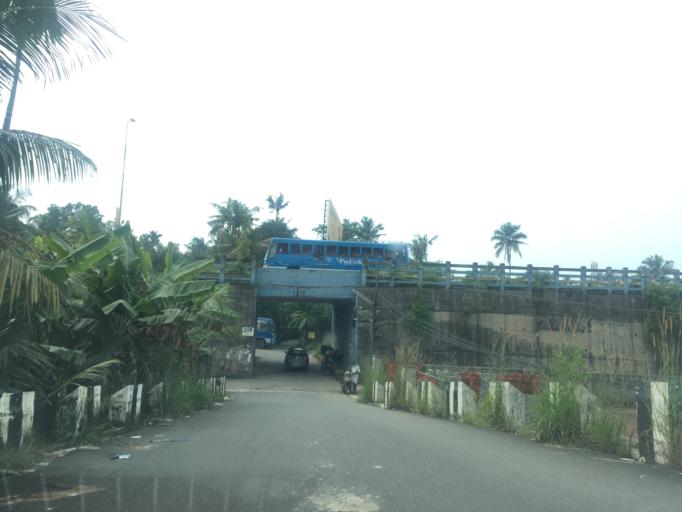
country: IN
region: Kerala
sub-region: Ernakulam
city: Elur
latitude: 10.0330
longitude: 76.3047
